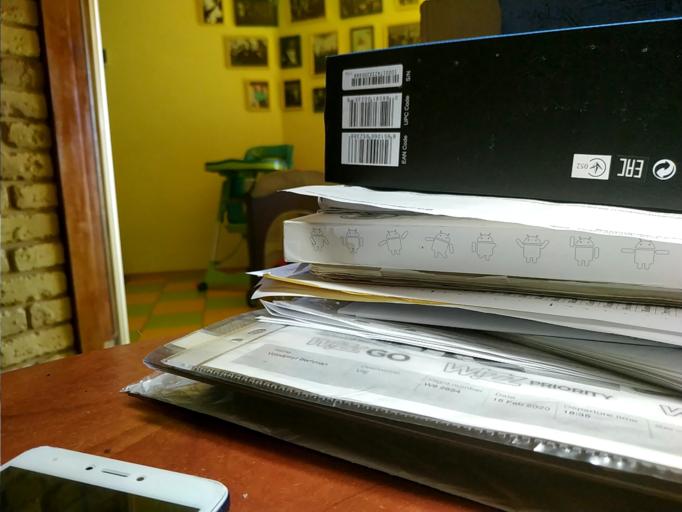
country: RU
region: Novgorod
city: Kholm
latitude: 59.2662
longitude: 32.7904
